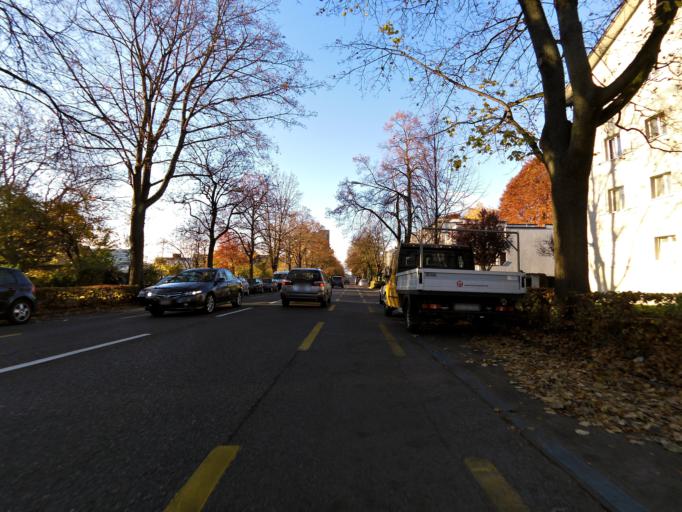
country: CH
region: Zurich
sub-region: Bezirk Zuerich
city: Zuerich (Kreis 3) / Sihlfeld
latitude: 47.3747
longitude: 8.5020
